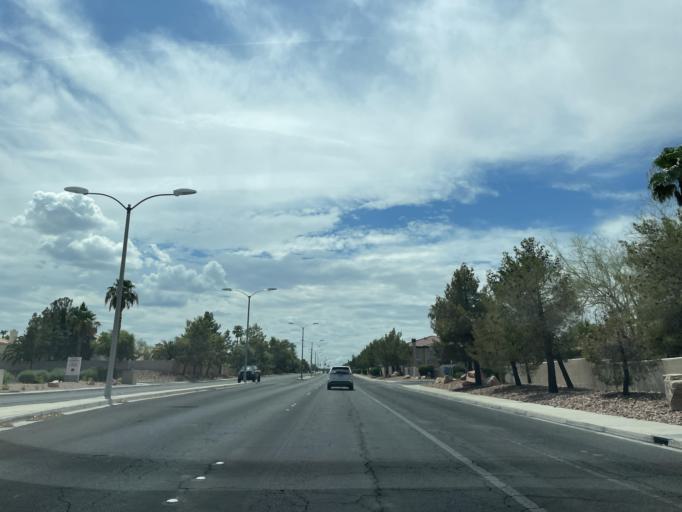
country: US
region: Nevada
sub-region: Clark County
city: Whitney
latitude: 36.0319
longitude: -115.1004
